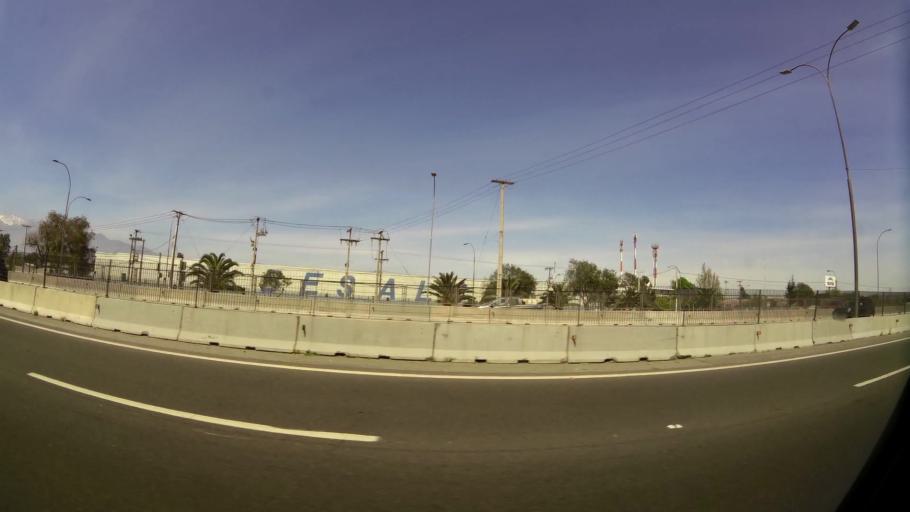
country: CL
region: Santiago Metropolitan
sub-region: Provincia de Maipo
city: San Bernardo
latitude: -33.5414
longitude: -70.6870
